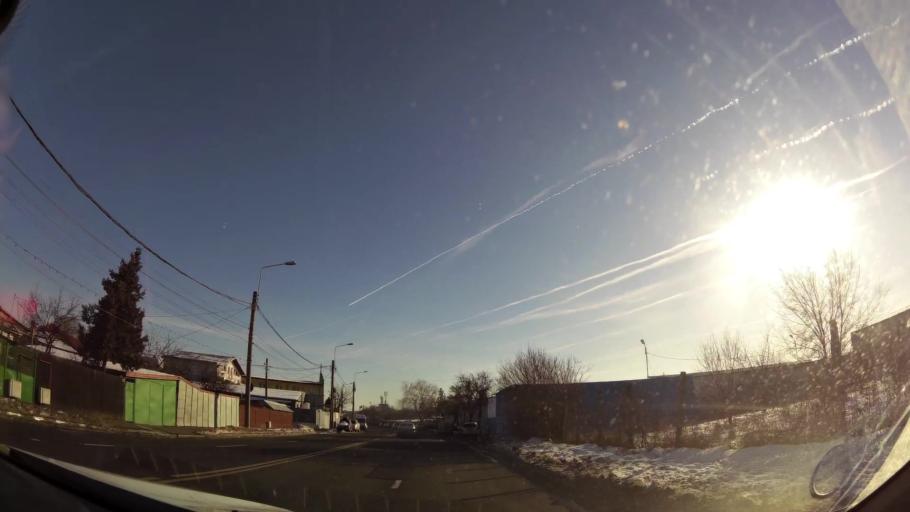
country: RO
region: Ilfov
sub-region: Comuna Fundeni-Dobroesti
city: Fundeni
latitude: 44.4780
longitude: 26.1389
